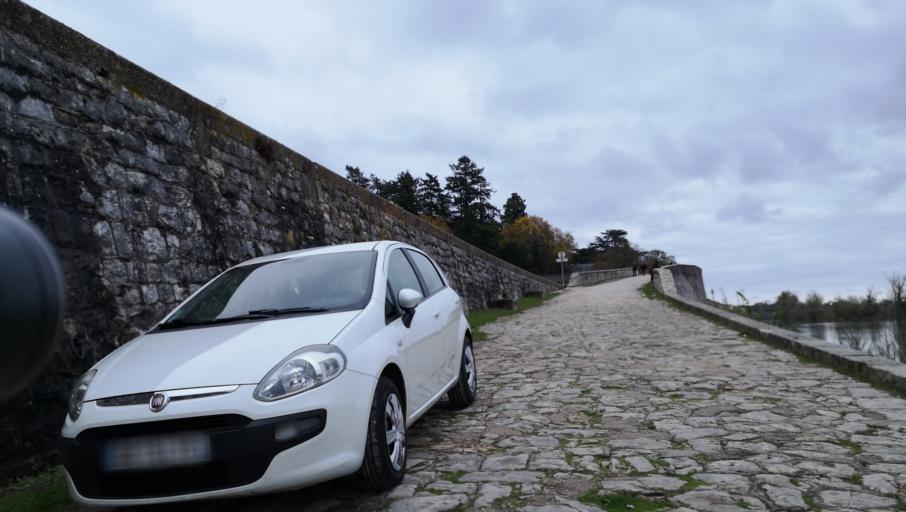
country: FR
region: Centre
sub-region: Departement du Loiret
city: Saint-Jean-le-Blanc
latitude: 47.9020
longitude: 1.9394
